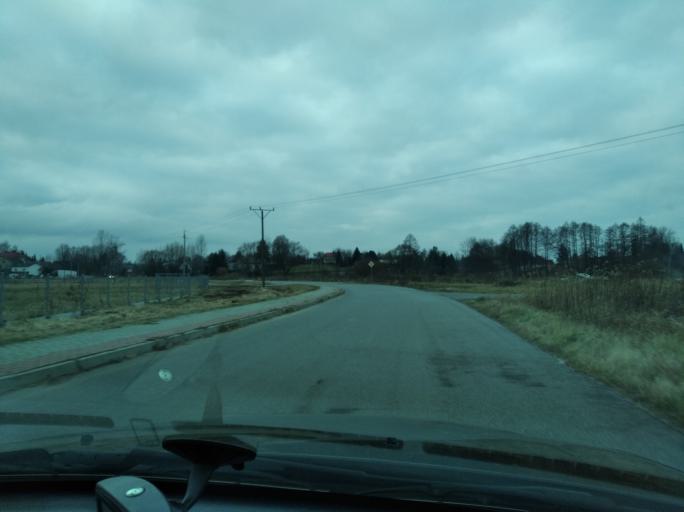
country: PL
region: Subcarpathian Voivodeship
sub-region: Powiat rzeszowski
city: Boguchwala
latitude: 49.9742
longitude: 21.9299
